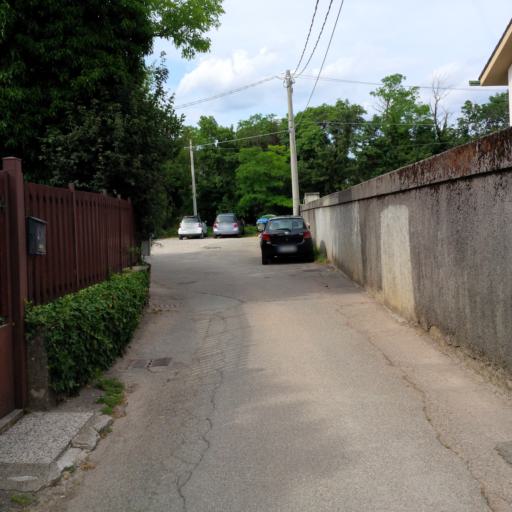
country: IT
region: Friuli Venezia Giulia
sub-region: Provincia di Trieste
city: Villa Opicina
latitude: 45.6868
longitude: 13.7999
